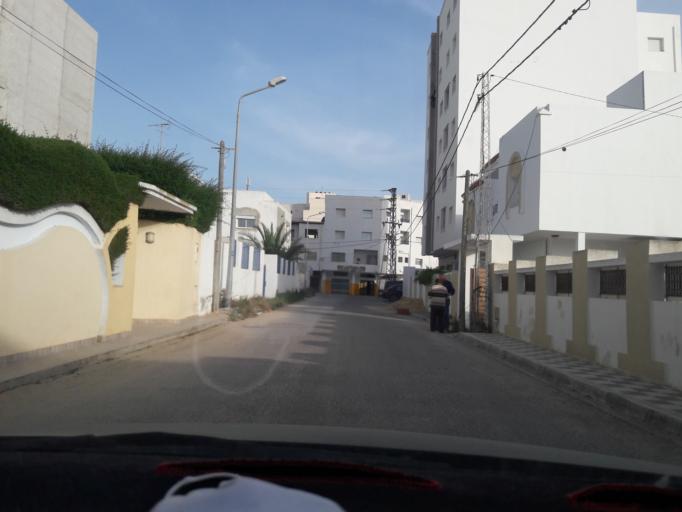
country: TN
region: Safaqis
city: Al Qarmadah
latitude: 34.8005
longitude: 10.7558
